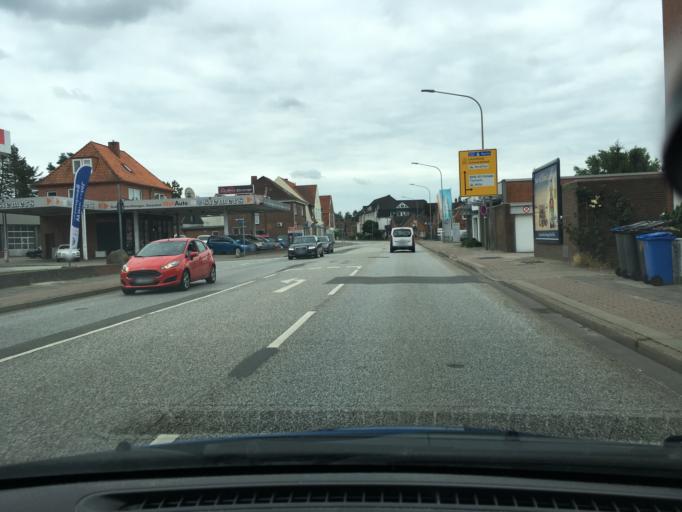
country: DE
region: Schleswig-Holstein
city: Geesthacht
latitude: 53.4443
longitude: 10.3628
